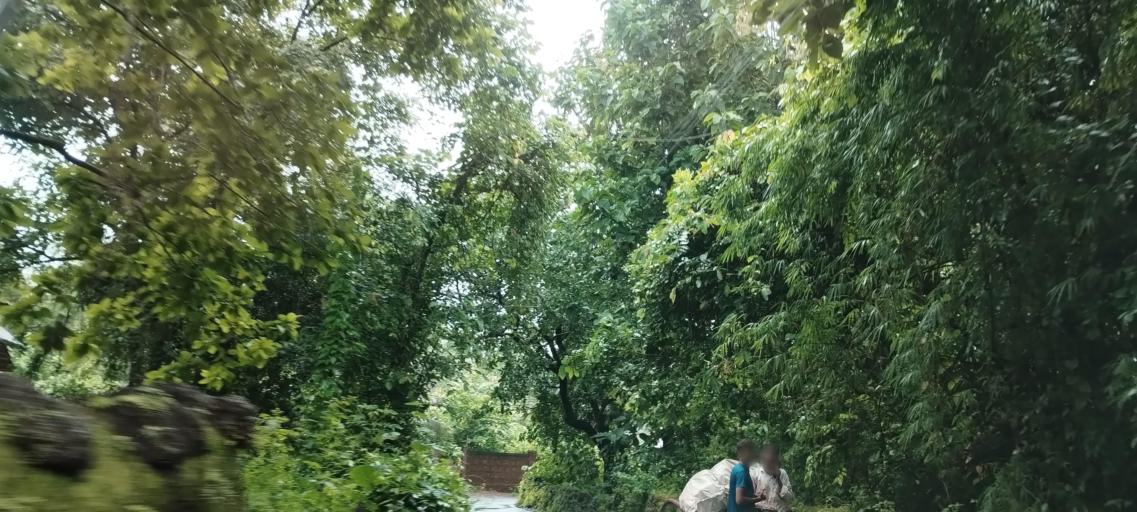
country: IN
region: Goa
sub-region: North Goa
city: Aldona
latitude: 15.5839
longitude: 73.8673
